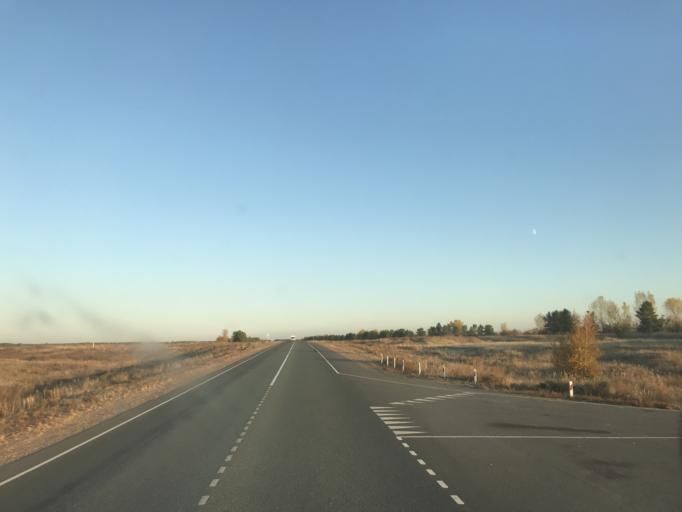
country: KZ
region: East Kazakhstan
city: Semey
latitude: 50.7580
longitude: 79.5973
